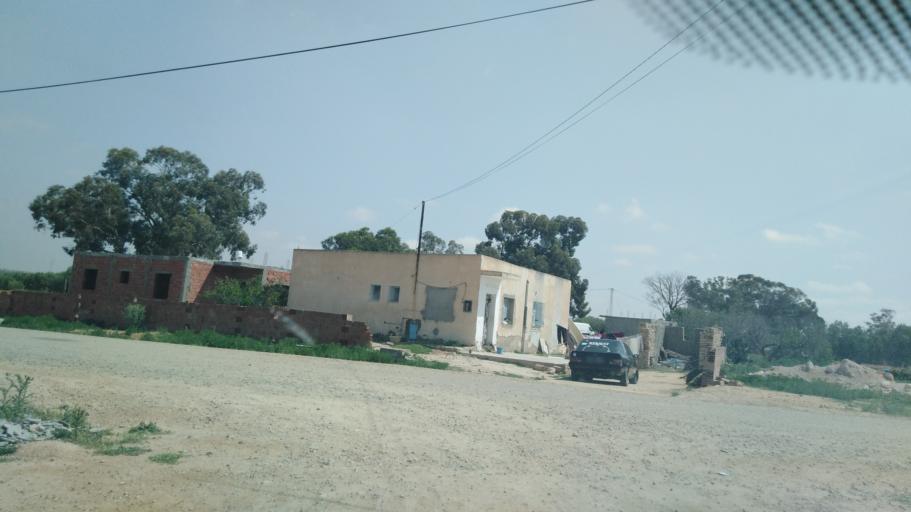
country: TN
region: Safaqis
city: Sfax
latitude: 34.7296
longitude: 10.5675
